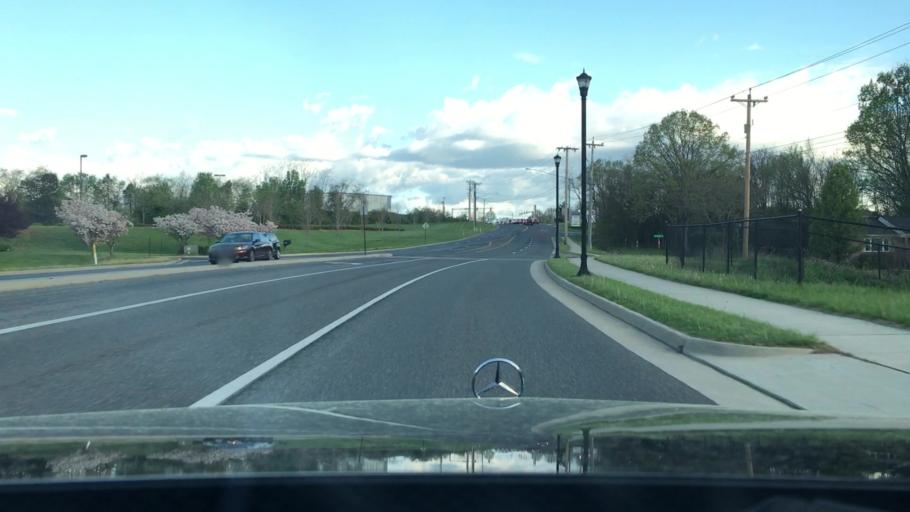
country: US
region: Virginia
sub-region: Campbell County
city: Timberlake
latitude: 37.3423
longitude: -79.2316
